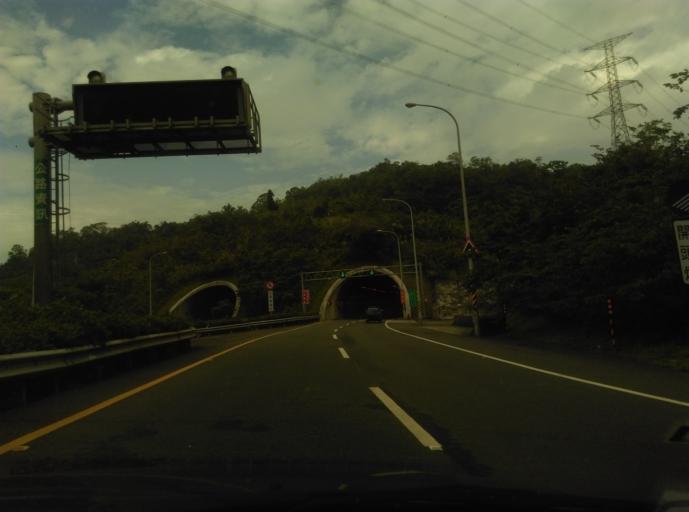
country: TW
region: Taiwan
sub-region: Keelung
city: Keelung
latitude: 25.1284
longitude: 121.6971
